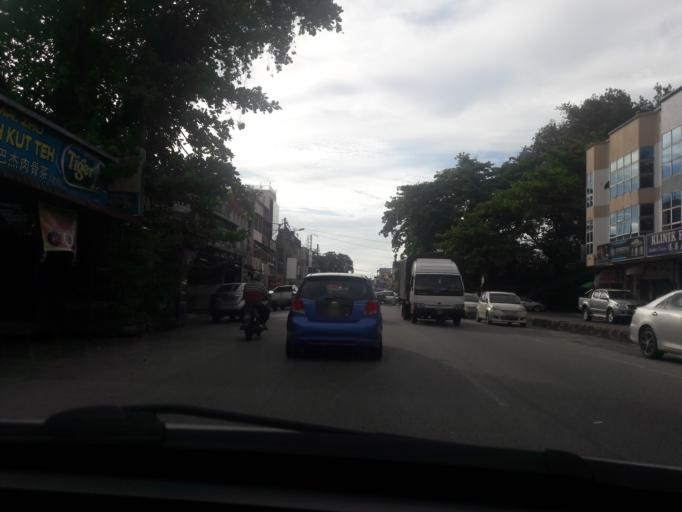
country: MY
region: Kedah
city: Sungai Petani
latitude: 5.6373
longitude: 100.4958
